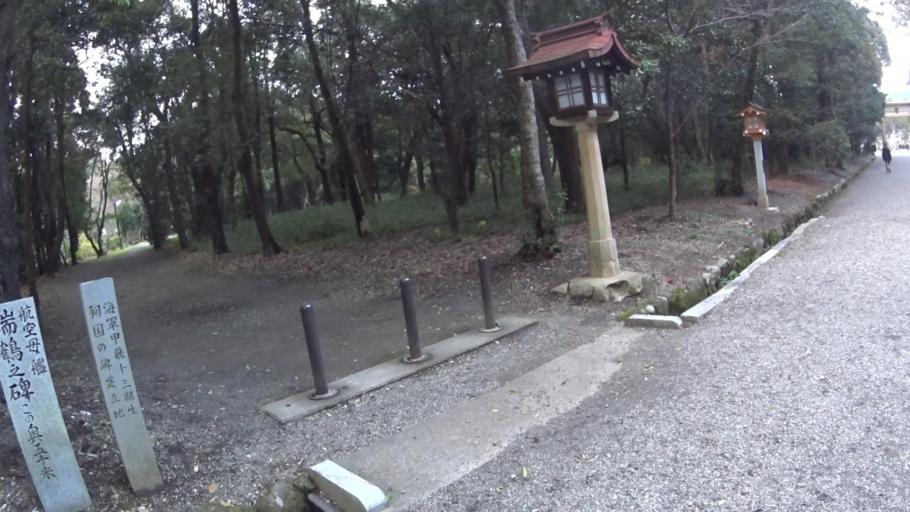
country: JP
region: Nara
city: Kashihara-shi
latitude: 34.4904
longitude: 135.7889
